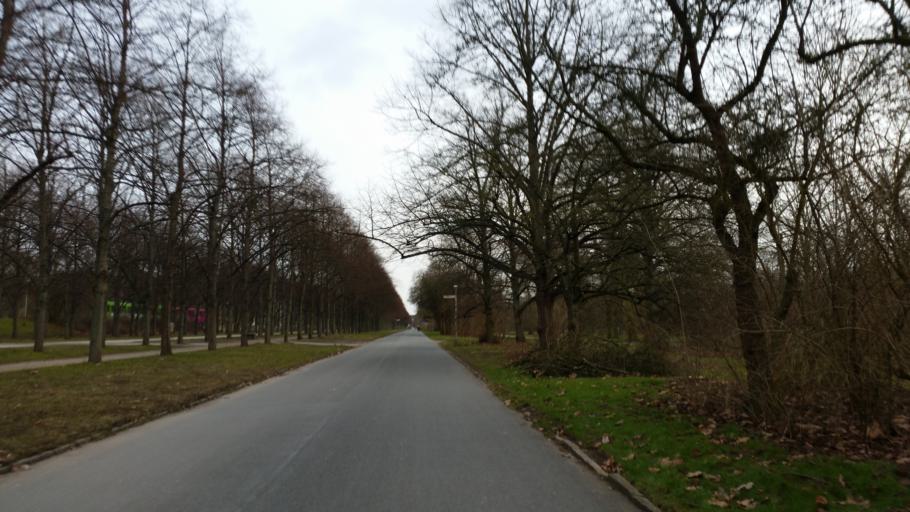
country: DE
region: Lower Saxony
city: Hannover
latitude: 52.3843
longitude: 9.7120
